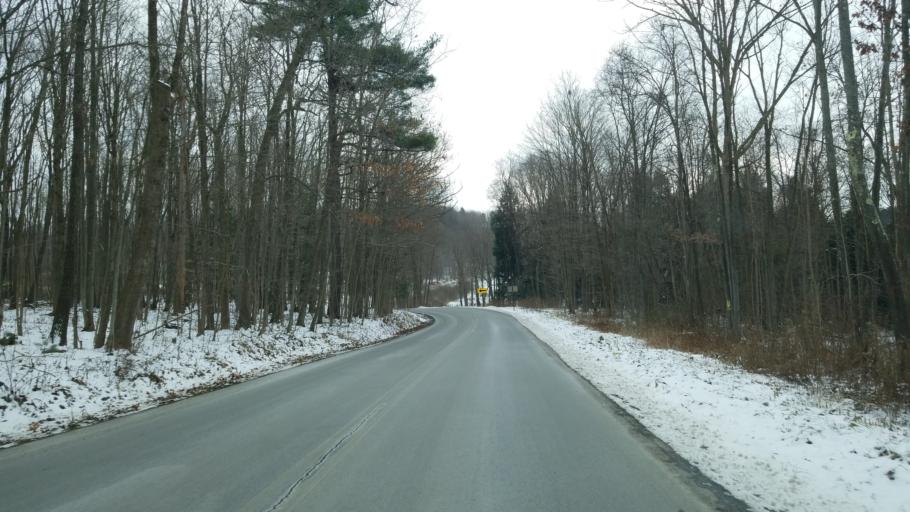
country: US
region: Pennsylvania
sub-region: Clearfield County
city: Sandy
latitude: 41.0917
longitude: -78.7502
